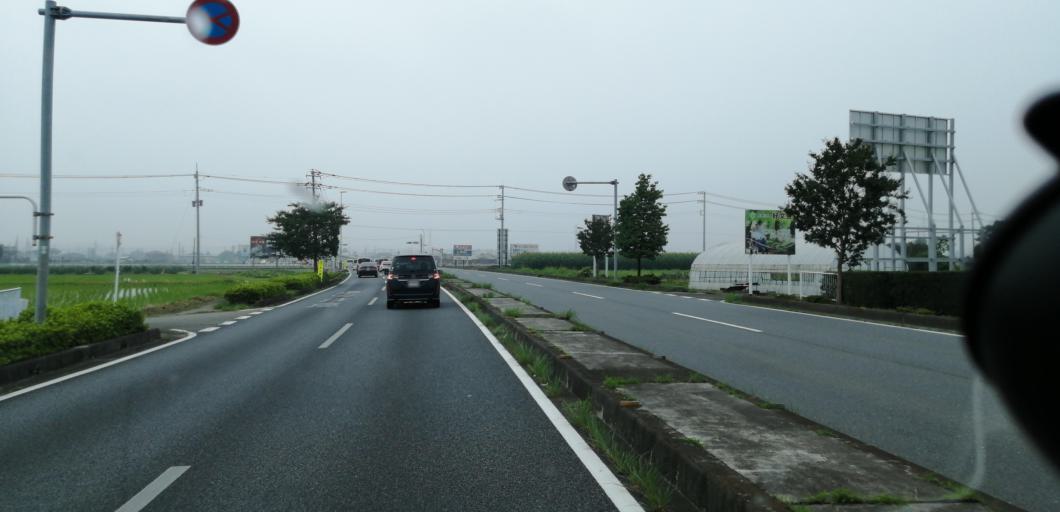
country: JP
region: Saitama
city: Yorii
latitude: 36.1373
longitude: 139.2527
